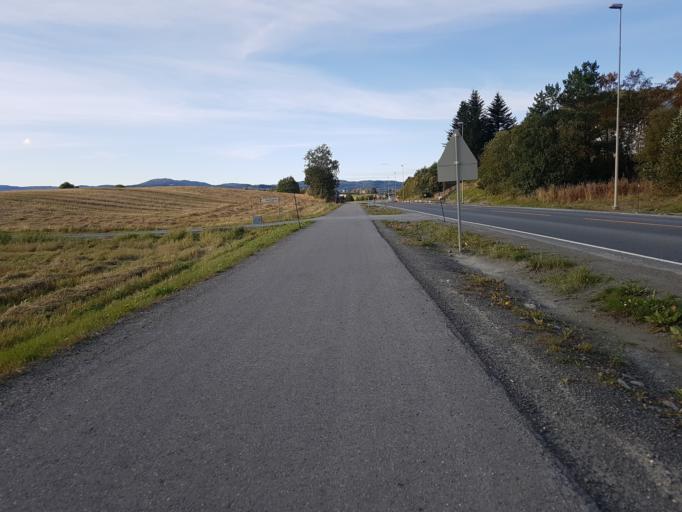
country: NO
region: Sor-Trondelag
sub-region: Trondheim
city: Trondheim
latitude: 63.3717
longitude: 10.4340
